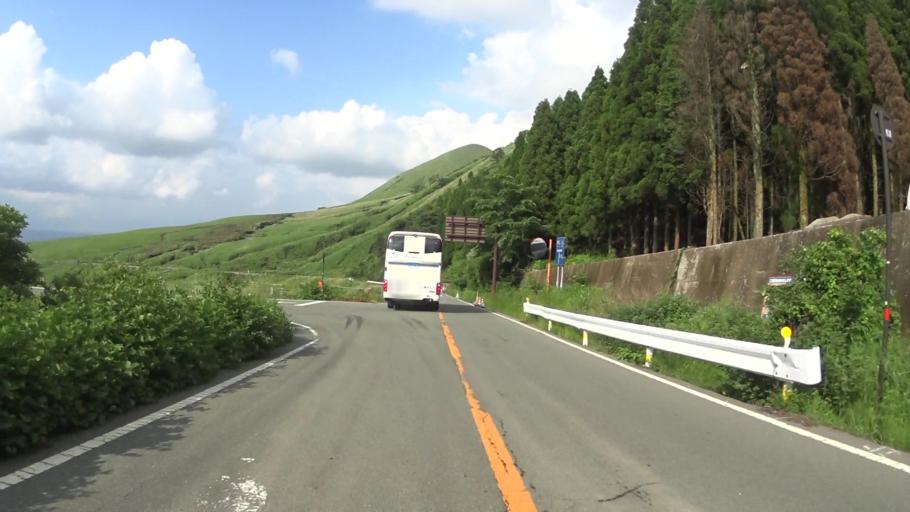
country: JP
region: Kumamoto
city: Aso
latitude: 32.8965
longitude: 131.0501
